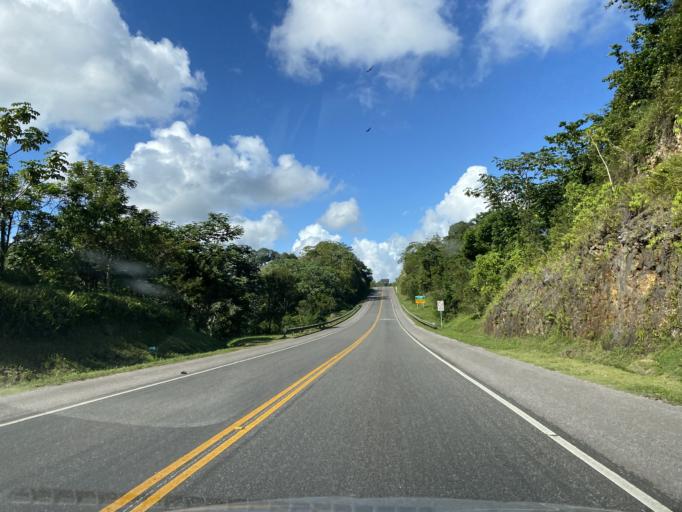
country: DO
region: Monte Plata
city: Majagual
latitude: 19.0342
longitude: -69.8267
